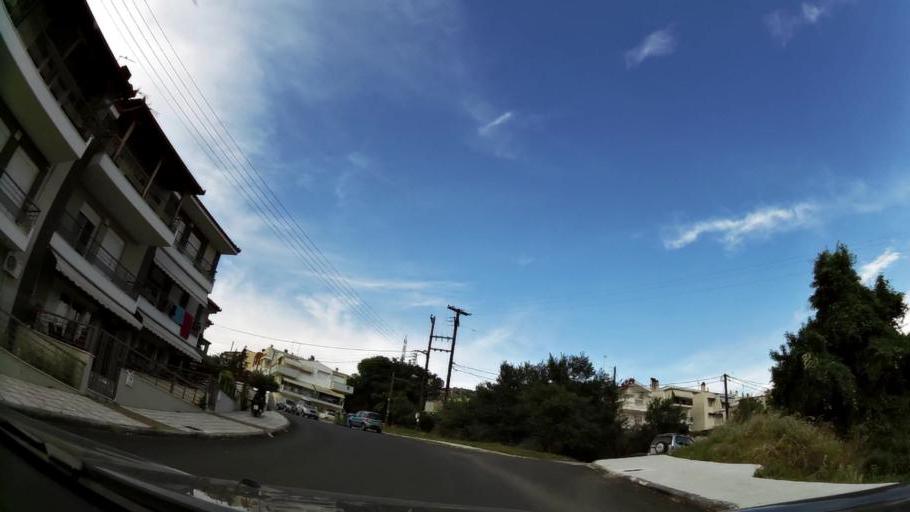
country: GR
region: Central Macedonia
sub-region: Nomos Thessalonikis
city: Pefka
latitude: 40.6551
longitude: 23.0016
